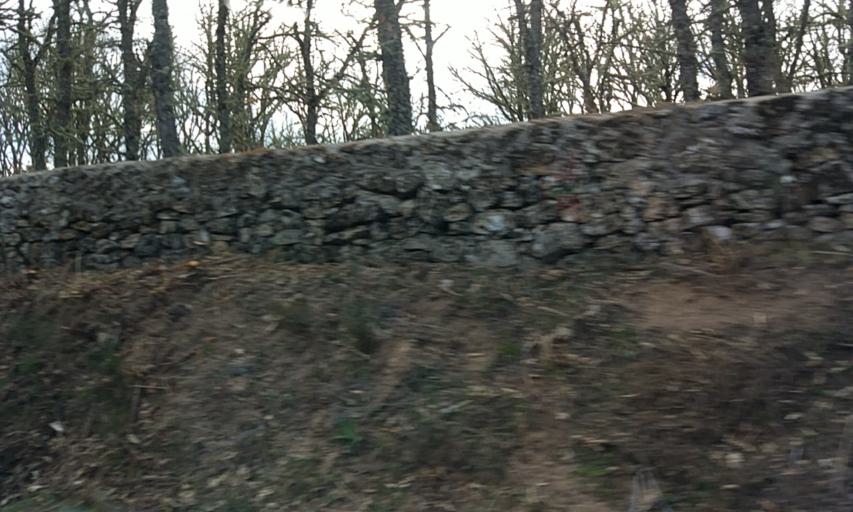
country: ES
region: Castille and Leon
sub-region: Provincia de Salamanca
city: Villasrubias
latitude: 40.3202
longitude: -6.6464
